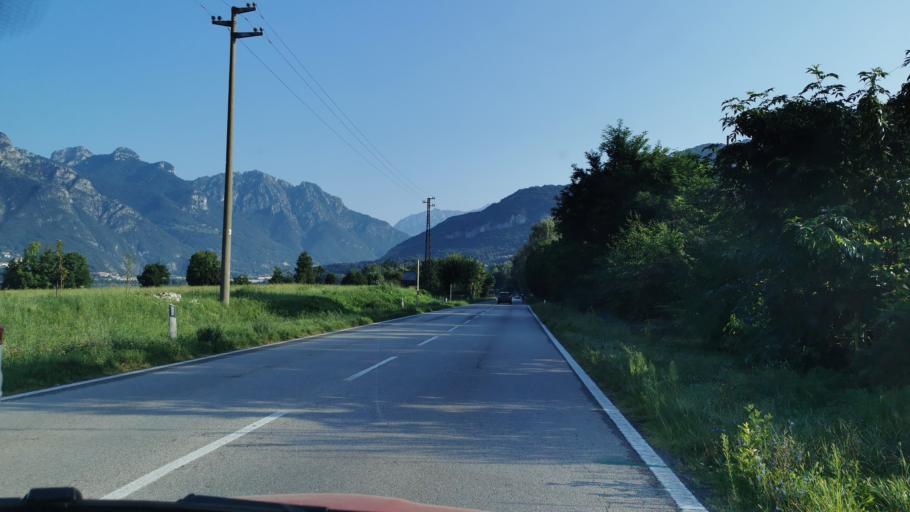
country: IT
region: Lombardy
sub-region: Provincia di Lecco
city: Sala al Barro
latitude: 45.8079
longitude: 9.3594
